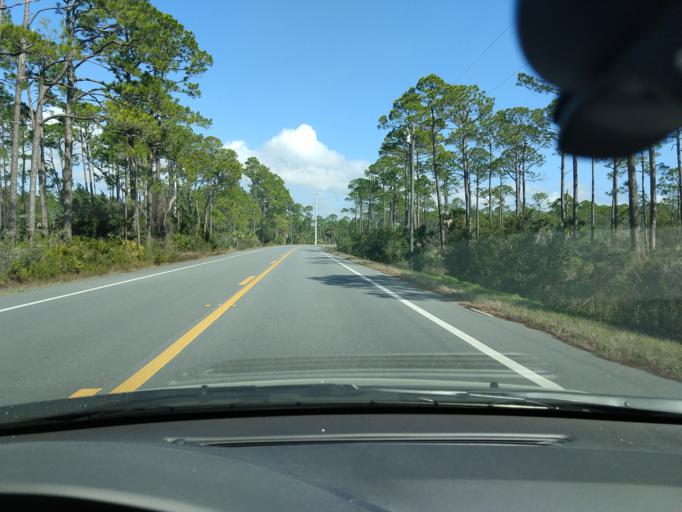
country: US
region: Florida
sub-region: Gulf County
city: Port Saint Joe
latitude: 29.6907
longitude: -85.2533
